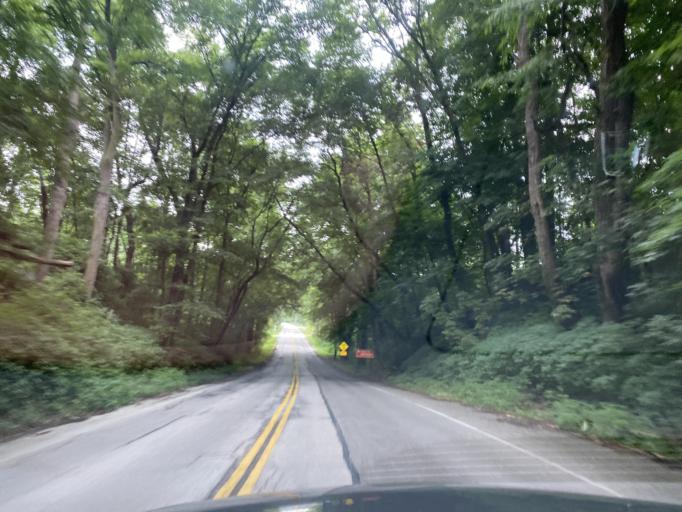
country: US
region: Ohio
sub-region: Summit County
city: Peninsula
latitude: 41.1926
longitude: -81.5791
